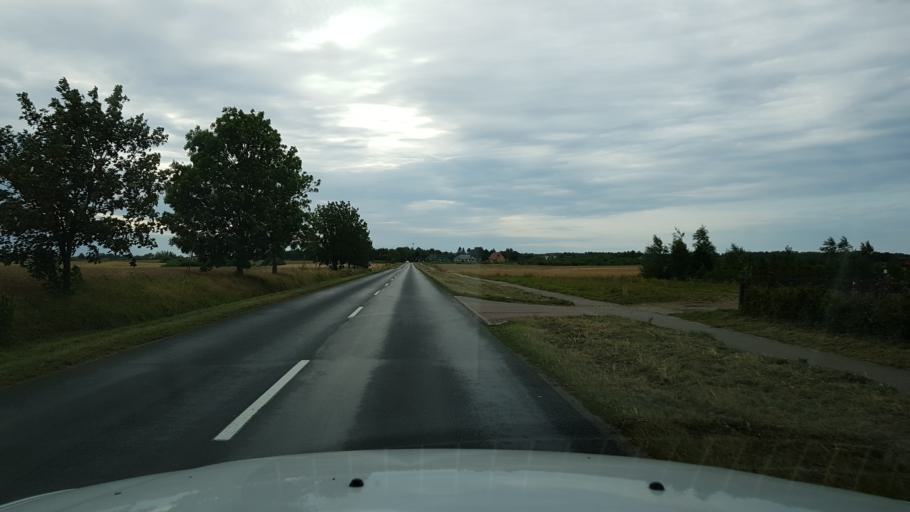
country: PL
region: West Pomeranian Voivodeship
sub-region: Powiat kolobrzeski
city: Dygowo
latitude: 54.1350
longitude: 15.7115
